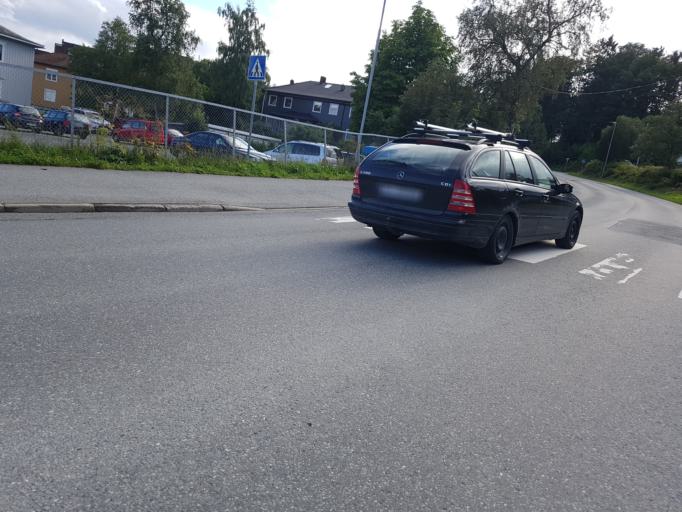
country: NO
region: Sor-Trondelag
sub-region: Trondheim
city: Trondheim
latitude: 63.4310
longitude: 10.4394
